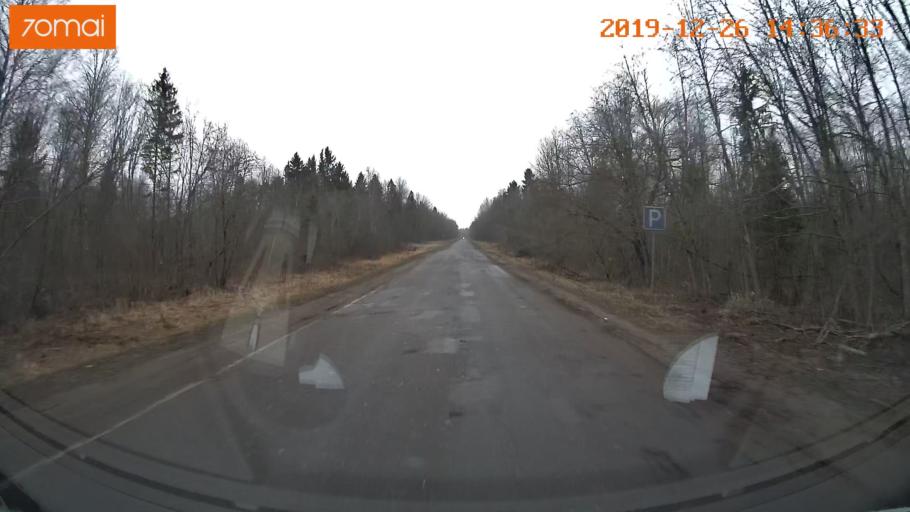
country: RU
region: Jaroslavl
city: Poshekhon'ye
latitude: 58.4102
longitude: 38.9756
